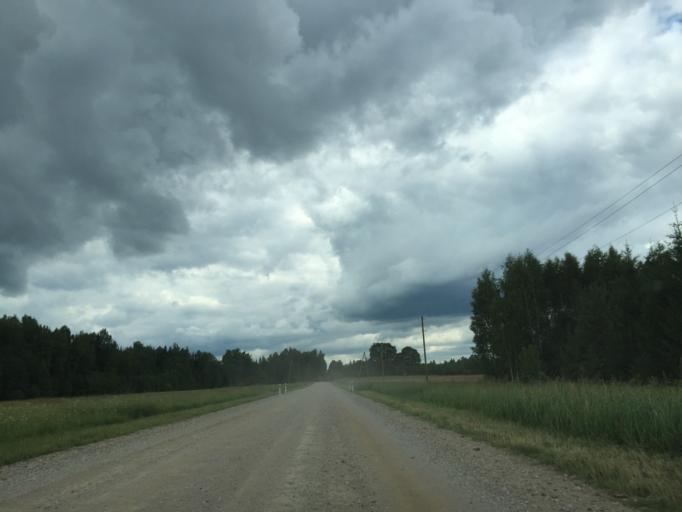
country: LV
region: Malpils
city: Malpils
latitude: 56.8687
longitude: 25.0090
